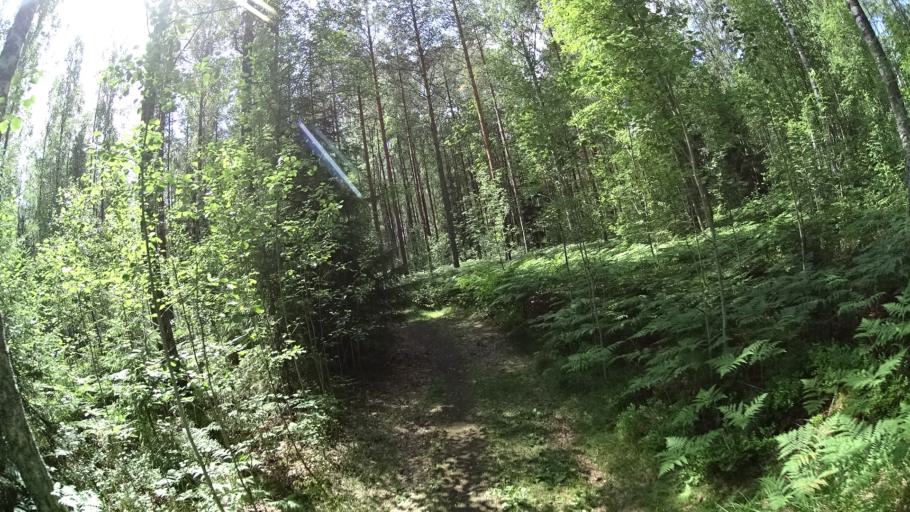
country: FI
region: Haeme
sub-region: Forssa
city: Tammela
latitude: 60.7721
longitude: 23.8679
